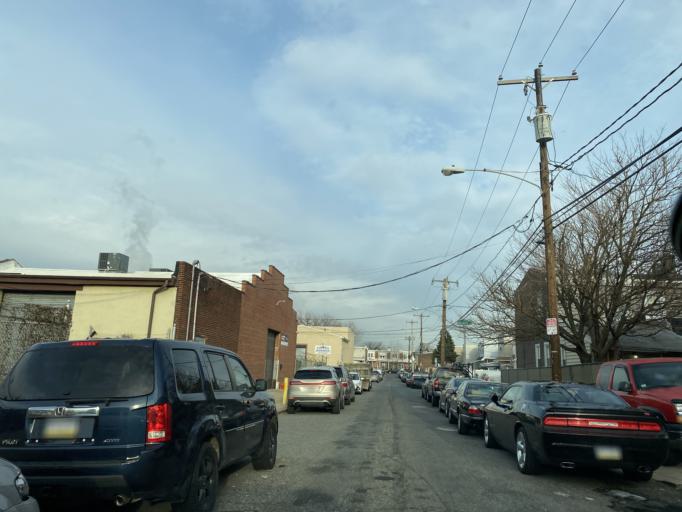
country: US
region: New Jersey
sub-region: Burlington County
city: Palmyra
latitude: 40.0014
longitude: -75.0754
